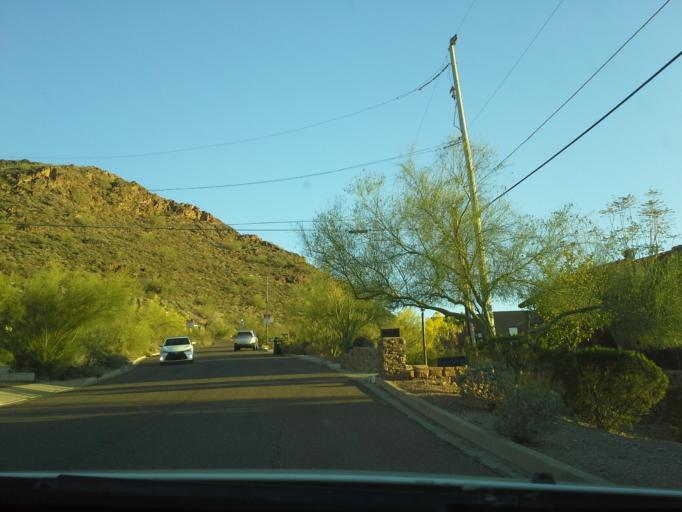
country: US
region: Arizona
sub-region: Maricopa County
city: Paradise Valley
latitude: 33.5693
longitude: -112.0482
